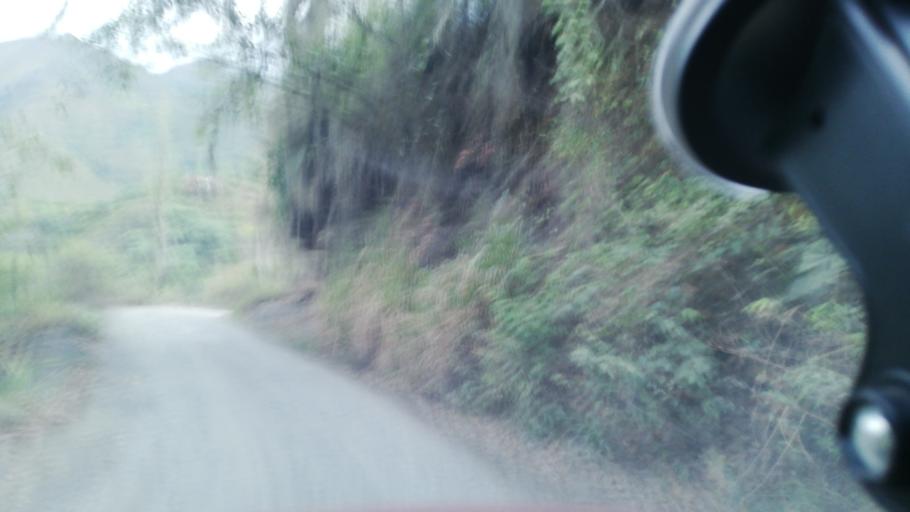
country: CO
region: Cundinamarca
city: Pacho
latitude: 5.1830
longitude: -74.1996
